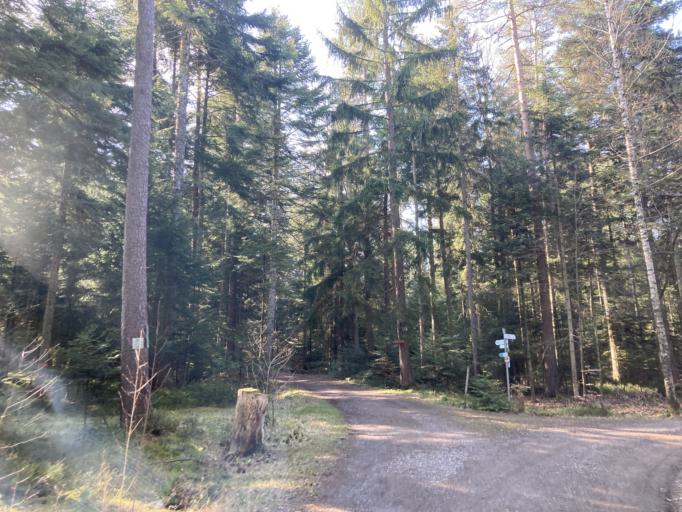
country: DE
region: Baden-Wuerttemberg
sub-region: Karlsruhe Region
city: Schomberg
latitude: 48.7771
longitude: 8.6406
